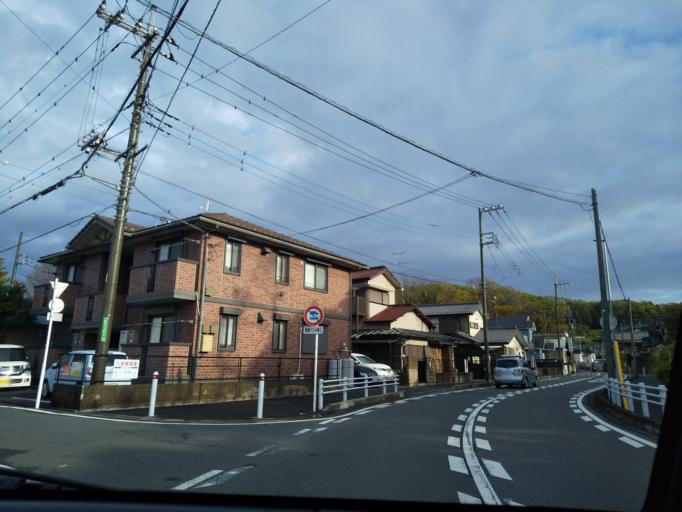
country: JP
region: Tokyo
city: Hachioji
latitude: 35.6046
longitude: 139.3189
